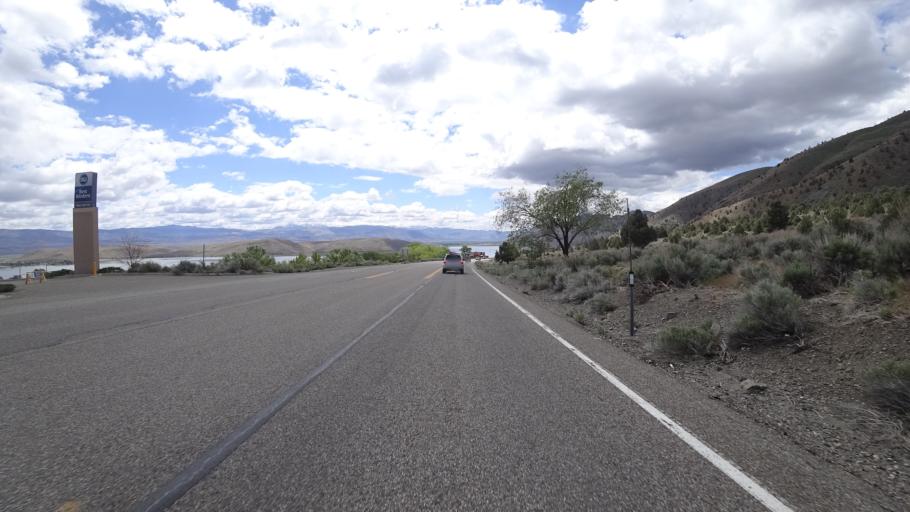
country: US
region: Nevada
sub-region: Lyon County
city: Smith Valley
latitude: 38.6985
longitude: -119.5501
